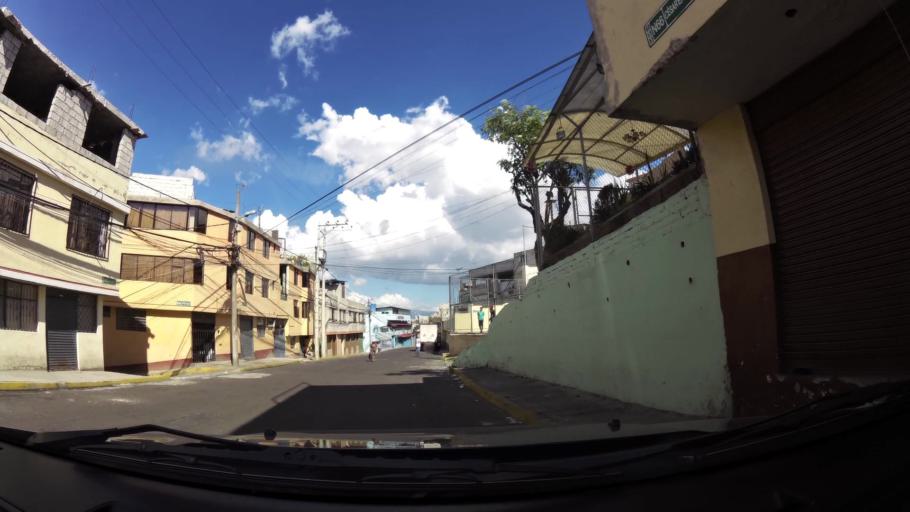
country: EC
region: Pichincha
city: Quito
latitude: -0.1198
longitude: -78.4645
